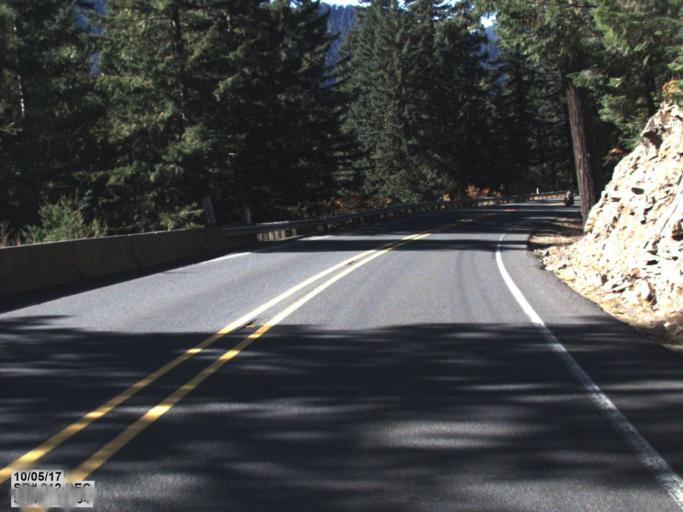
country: US
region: Washington
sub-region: Pierce County
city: Buckley
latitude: 46.6710
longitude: -121.5040
